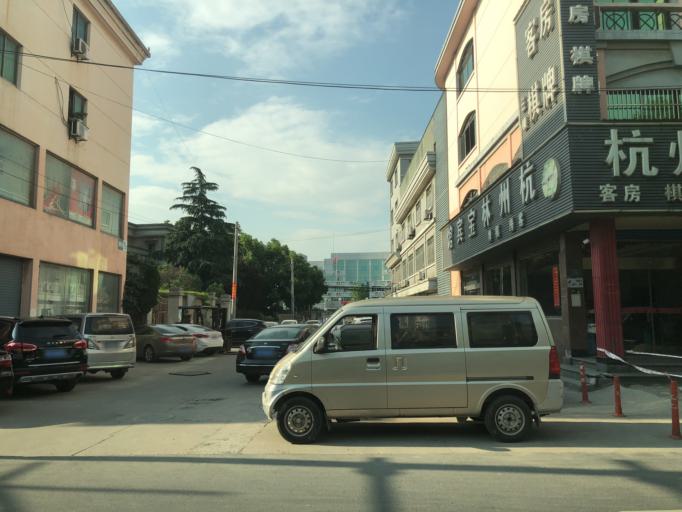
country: CN
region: Zhejiang Sheng
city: Qiaosi
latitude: 30.3503
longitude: 120.2820
